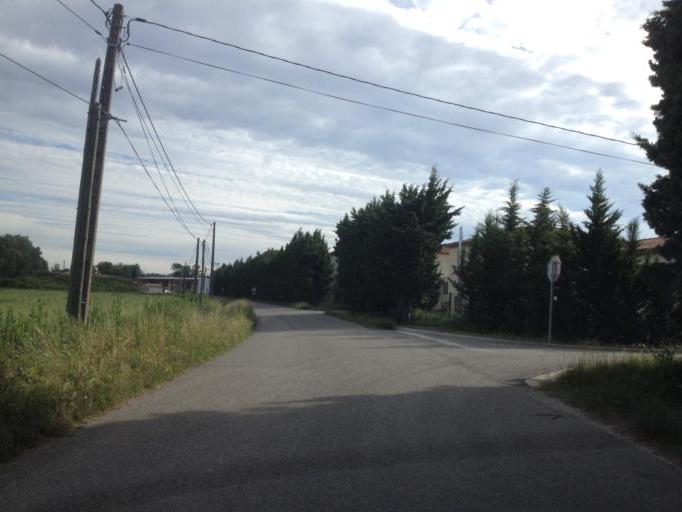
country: FR
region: Provence-Alpes-Cote d'Azur
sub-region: Departement du Vaucluse
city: Orange
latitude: 44.1236
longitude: 4.7920
